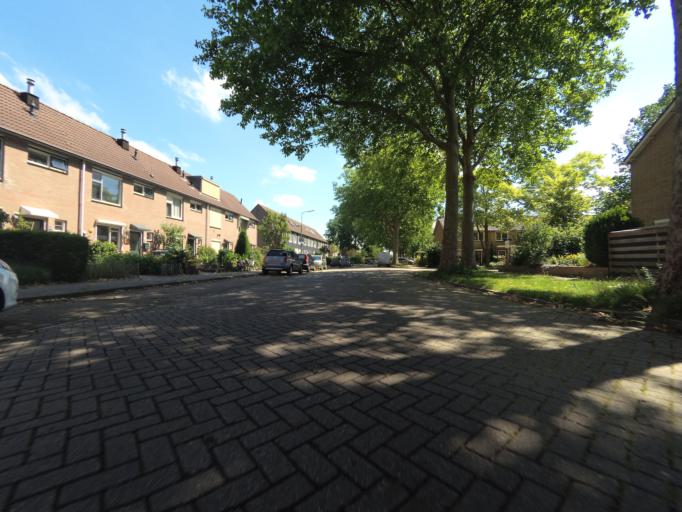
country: NL
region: Utrecht
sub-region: Gemeente Zeist
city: Zeist
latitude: 52.0530
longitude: 5.2364
